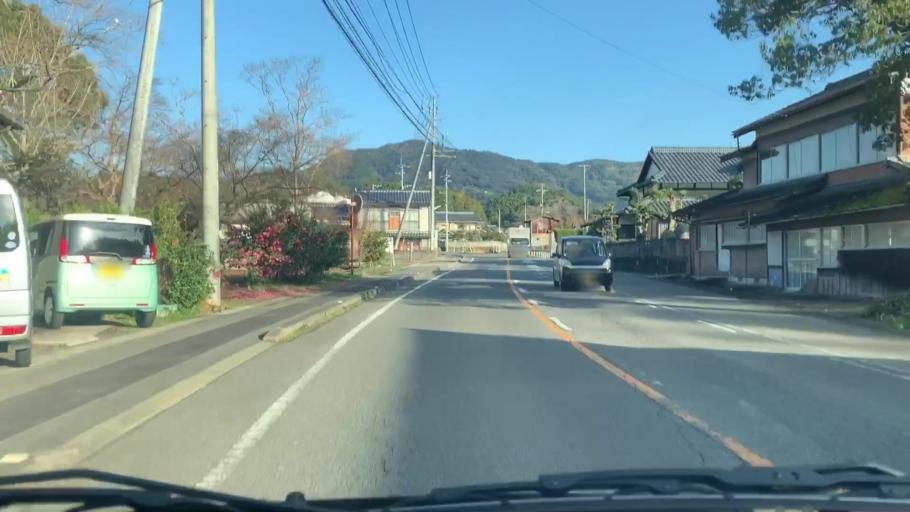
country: JP
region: Saga Prefecture
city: Takeocho-takeo
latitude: 33.2239
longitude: 130.0255
